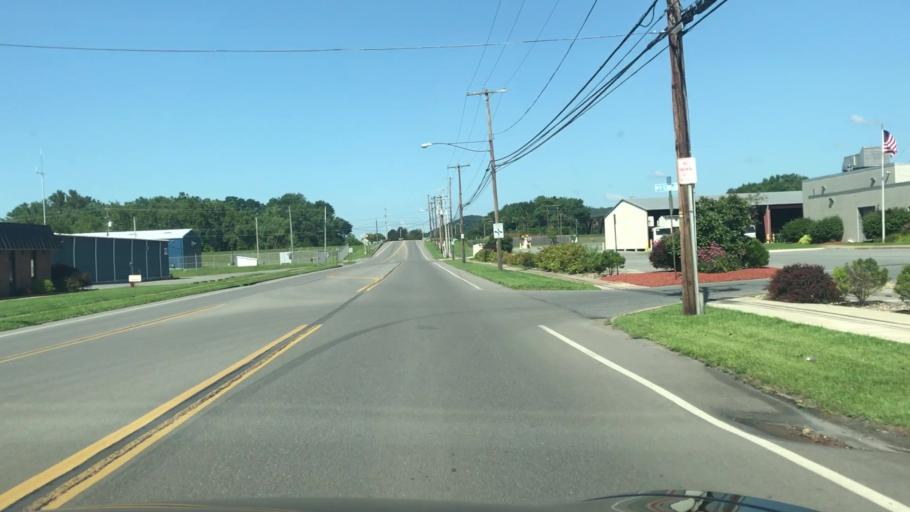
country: US
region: Pennsylvania
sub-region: Lycoming County
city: Duboistown
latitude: 41.2370
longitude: -77.0385
